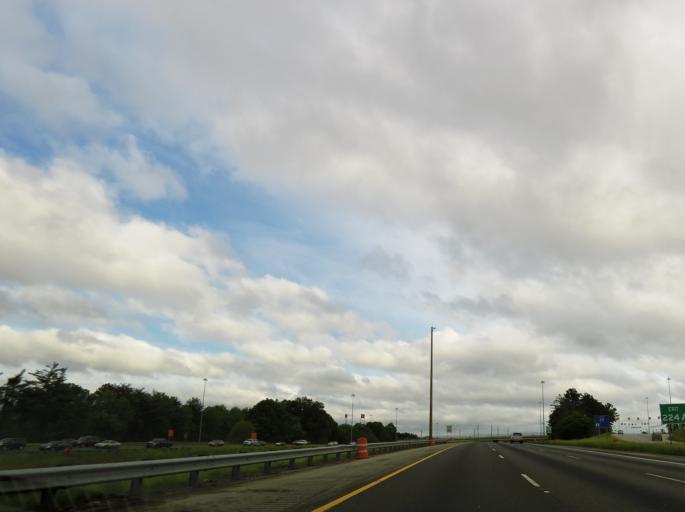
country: US
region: Georgia
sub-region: Henry County
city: Stockbridge
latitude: 33.5087
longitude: -84.2344
